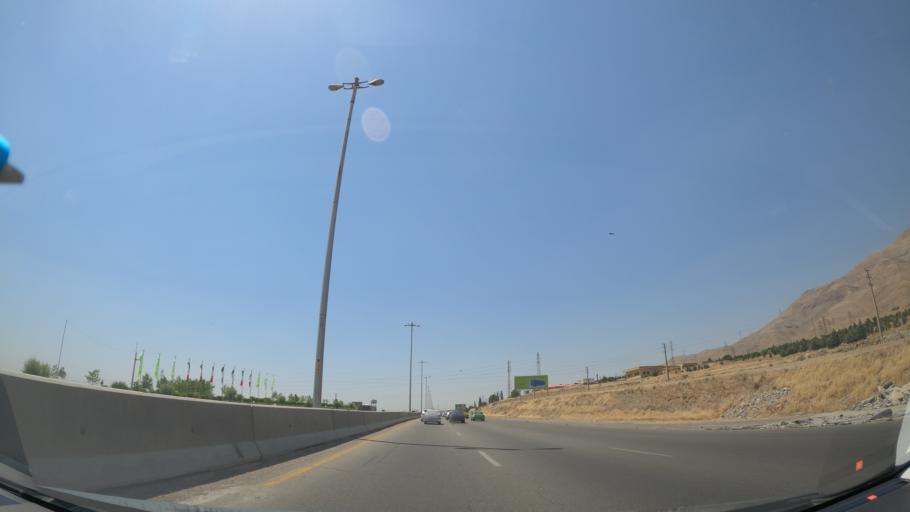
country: IR
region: Tehran
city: Shahr-e Qods
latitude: 35.7592
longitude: 51.0667
